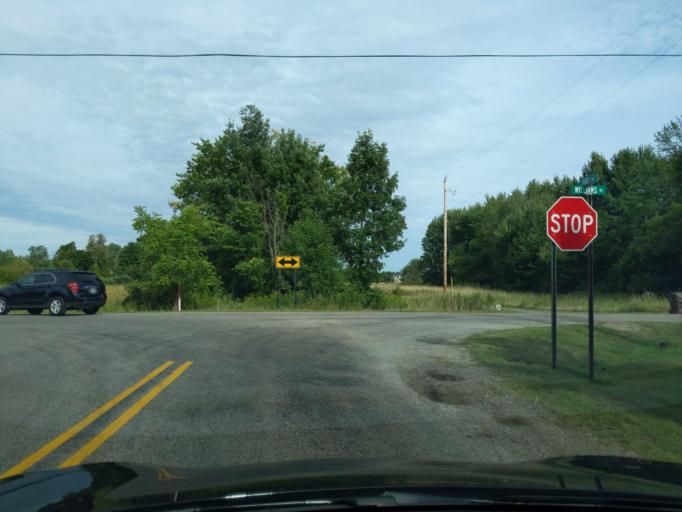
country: US
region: Michigan
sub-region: Eaton County
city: Dimondale
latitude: 42.6692
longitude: -84.6261
